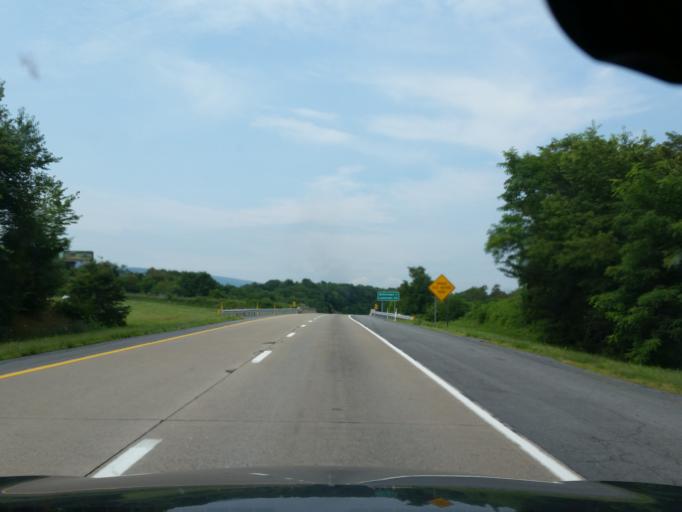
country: US
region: Pennsylvania
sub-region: Juniata County
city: Mifflintown
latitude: 40.5678
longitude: -77.2496
